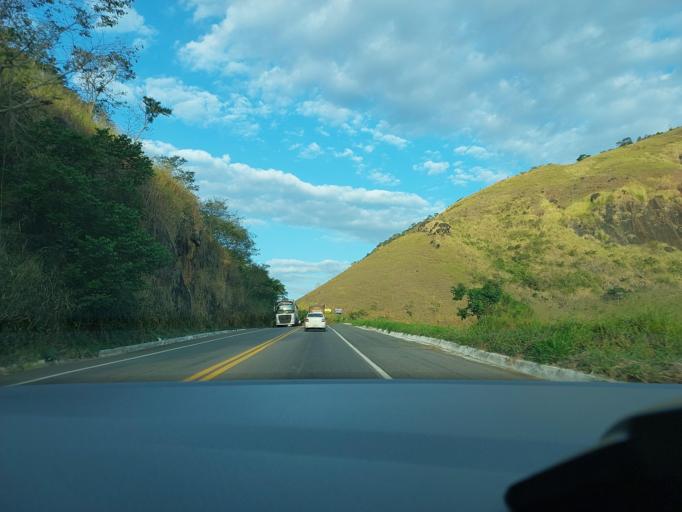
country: BR
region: Minas Gerais
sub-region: Muriae
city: Muriae
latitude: -21.1256
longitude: -42.2520
